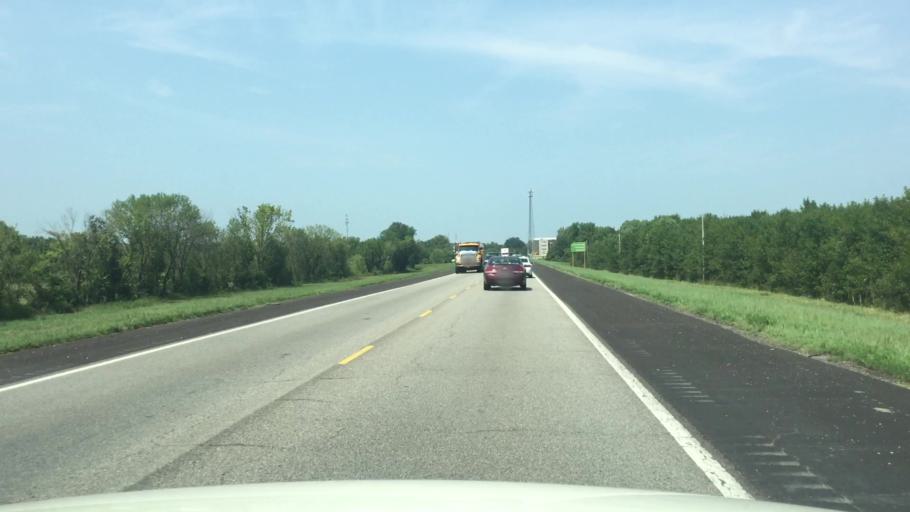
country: US
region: Kansas
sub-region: Crawford County
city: Pittsburg
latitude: 37.3749
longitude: -94.7081
